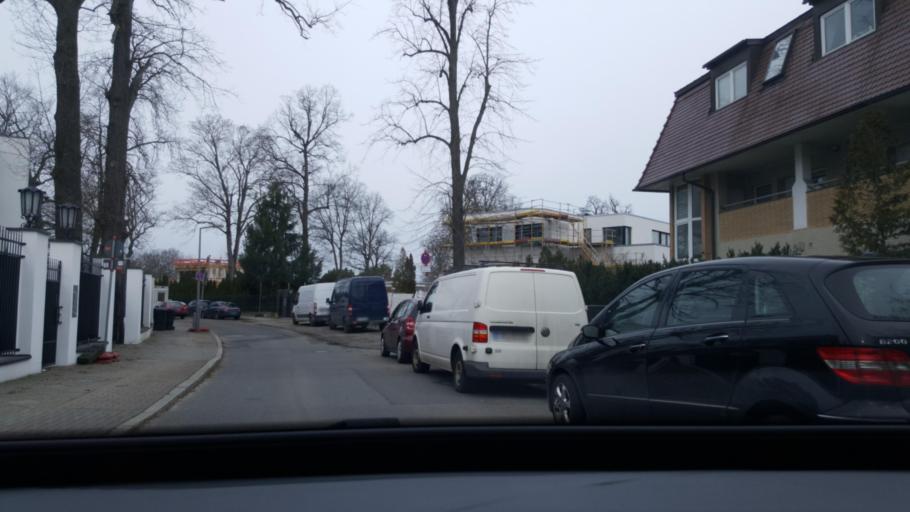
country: DE
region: Berlin
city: Wannsee
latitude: 52.4208
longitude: 13.1670
